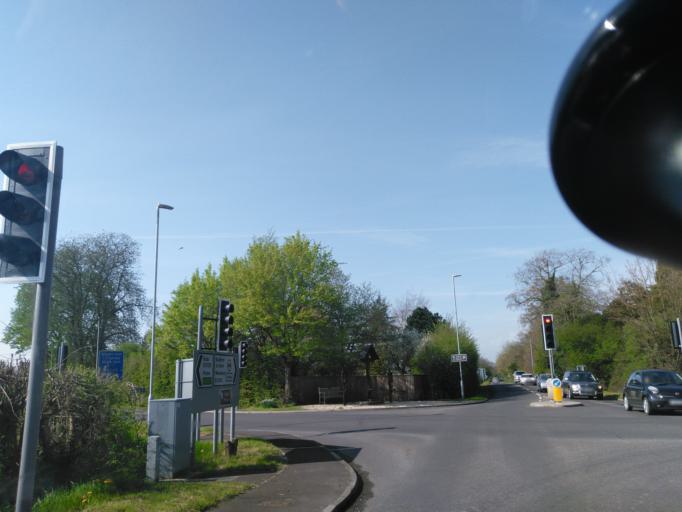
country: GB
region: England
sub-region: Wiltshire
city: Wingfield
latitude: 51.3142
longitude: -2.2574
